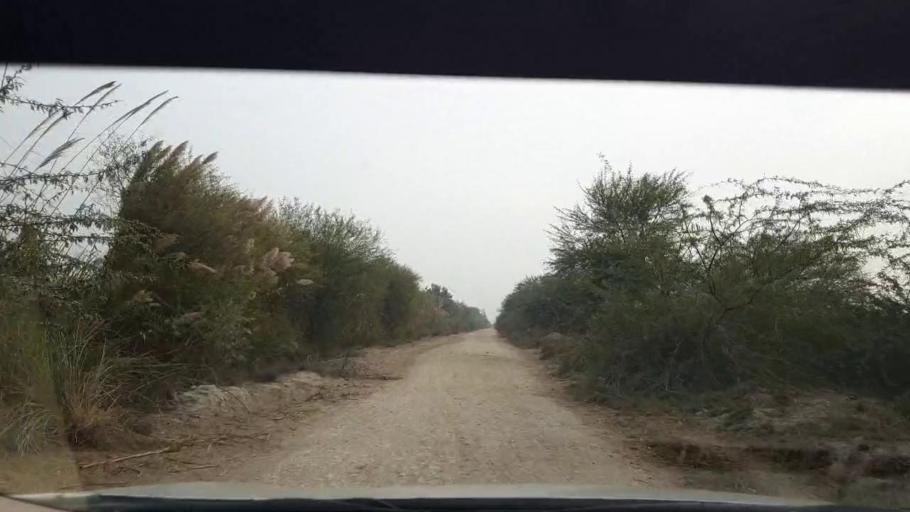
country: PK
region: Sindh
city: Berani
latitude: 25.8637
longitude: 68.8299
